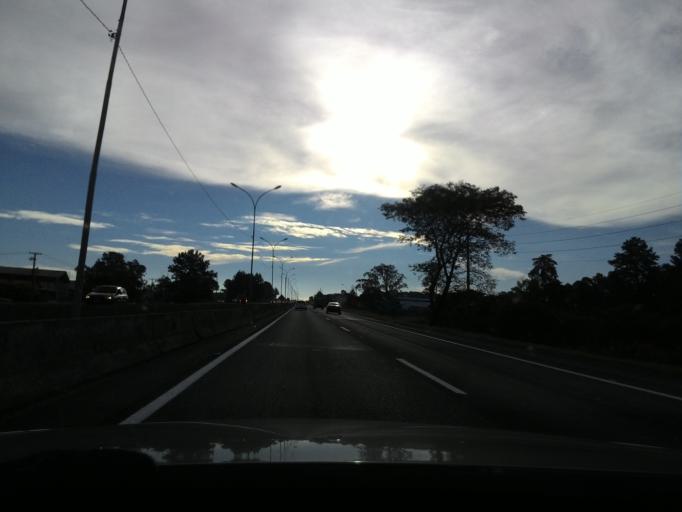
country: BR
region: Parana
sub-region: Quatro Barras
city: Quatro Barras
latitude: -25.3707
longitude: -49.1251
